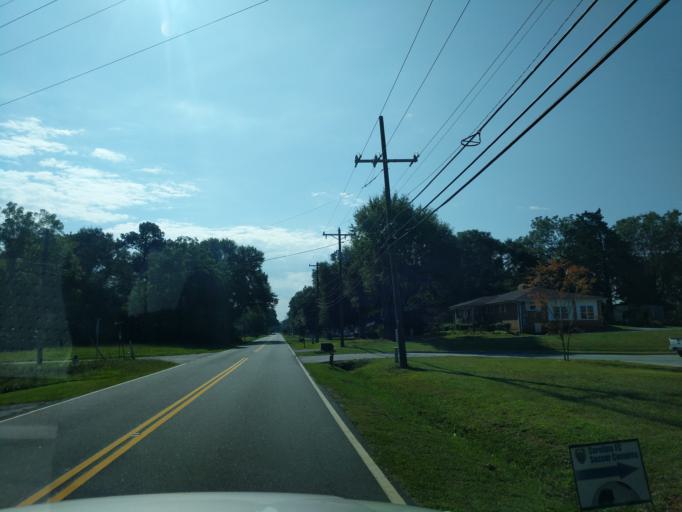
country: US
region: South Carolina
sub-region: Spartanburg County
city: Wellford
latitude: 34.9509
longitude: -82.1101
